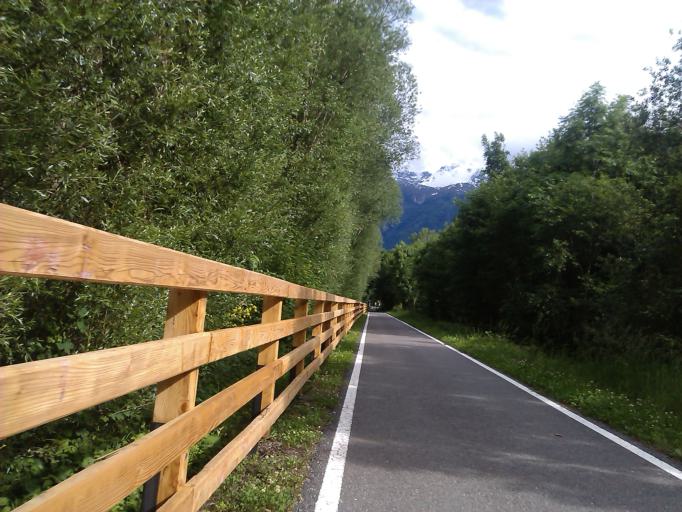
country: IT
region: Trentino-Alto Adige
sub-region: Bolzano
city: Sluderno
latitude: 46.6547
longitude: 10.5705
